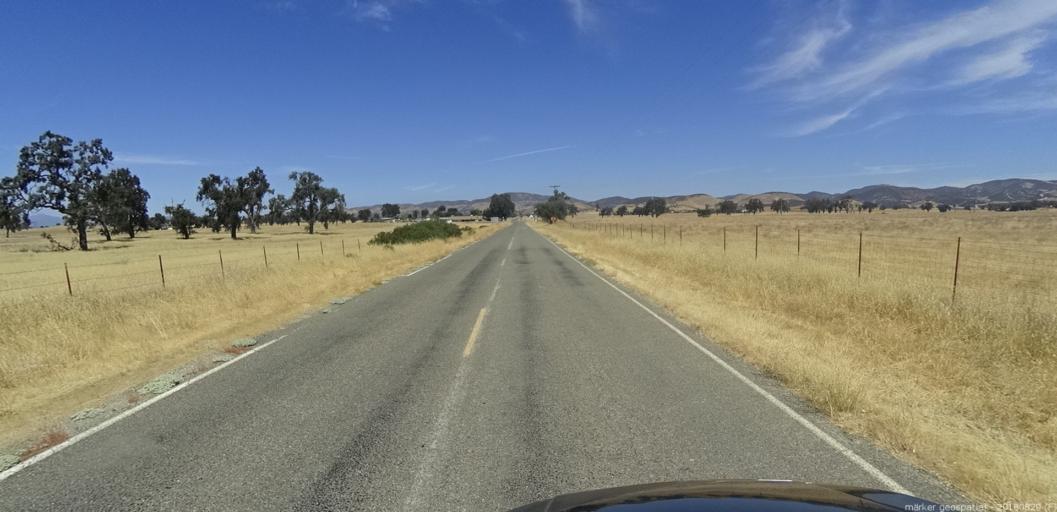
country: US
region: California
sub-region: Monterey County
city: King City
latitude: 35.9336
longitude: -121.0822
